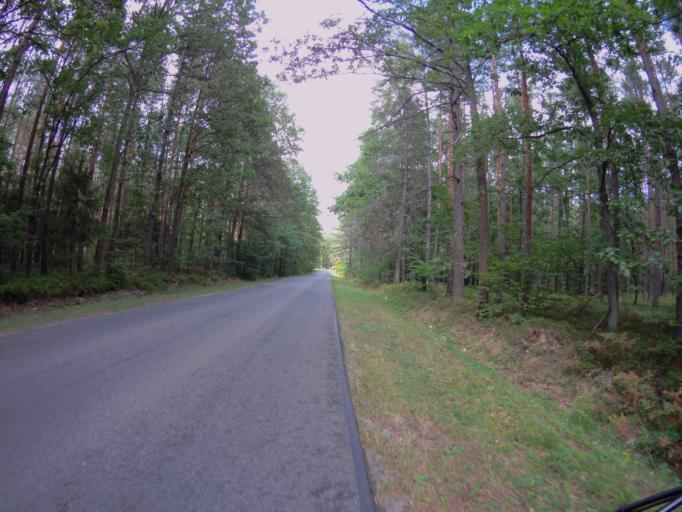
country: PL
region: Subcarpathian Voivodeship
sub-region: Powiat lezajski
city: Brzoza Krolewska
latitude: 50.2598
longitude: 22.3672
